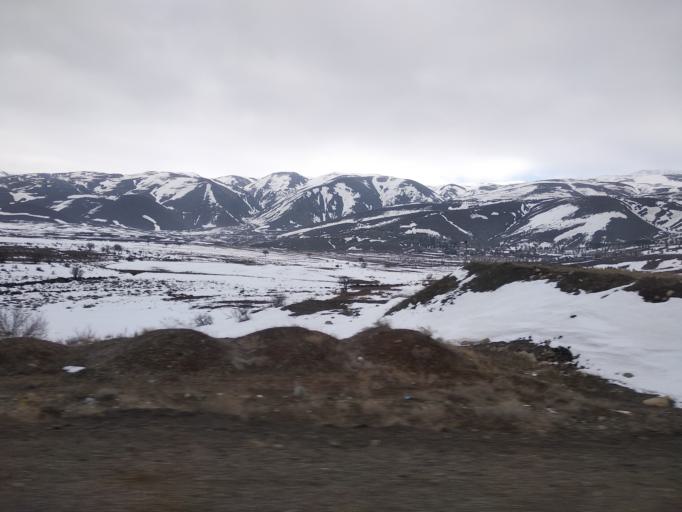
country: TR
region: Erzincan
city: Catalarmut
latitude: 39.8230
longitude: 39.4016
